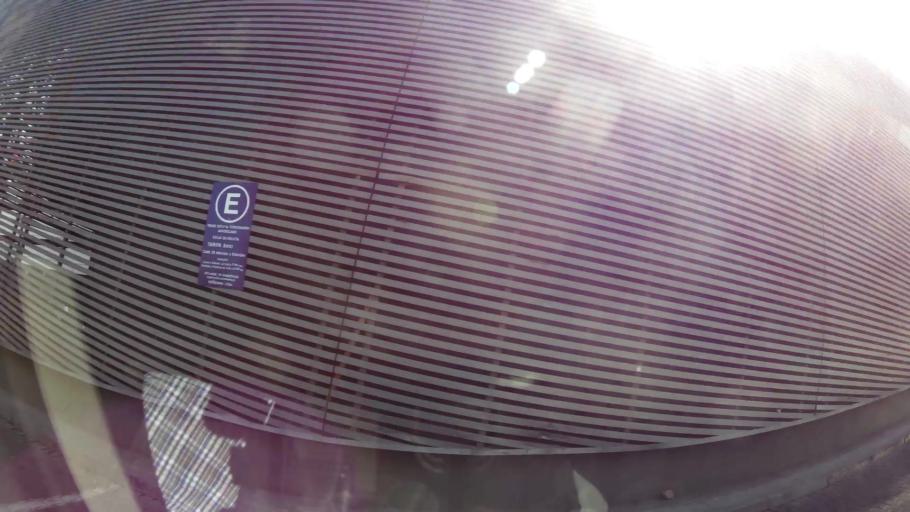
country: CL
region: Santiago Metropolitan
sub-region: Provincia de Santiago
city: Villa Presidente Frei, Nunoa, Santiago, Chile
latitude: -33.4107
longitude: -70.5673
